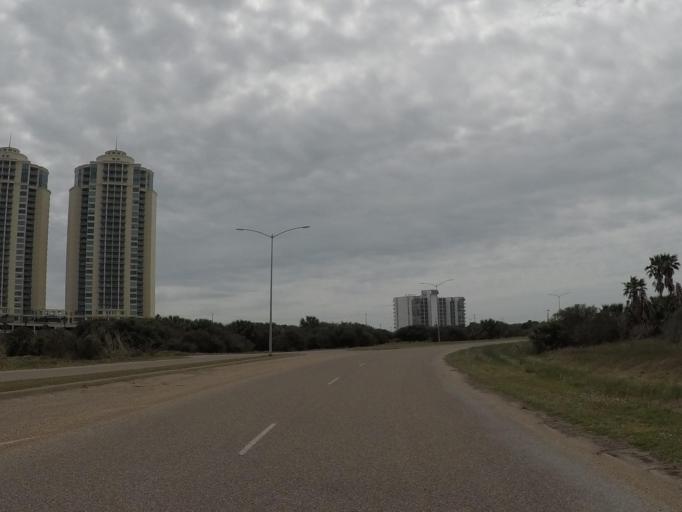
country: US
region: Texas
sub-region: Galveston County
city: Galveston
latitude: 29.3185
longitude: -94.7560
